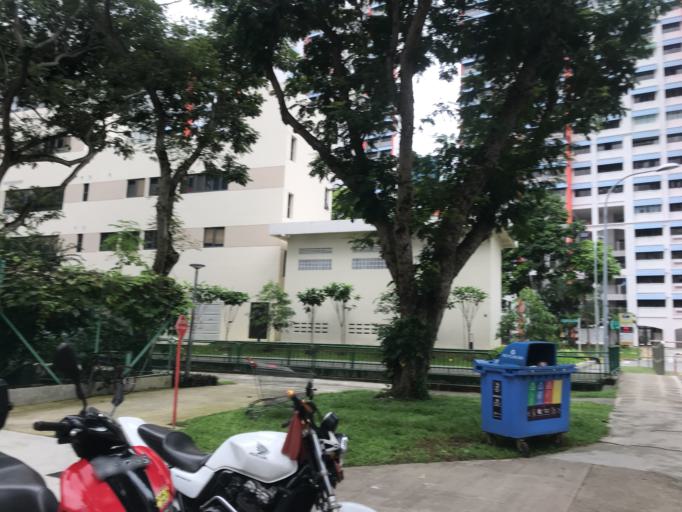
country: SG
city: Singapore
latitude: 1.3076
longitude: 103.8610
